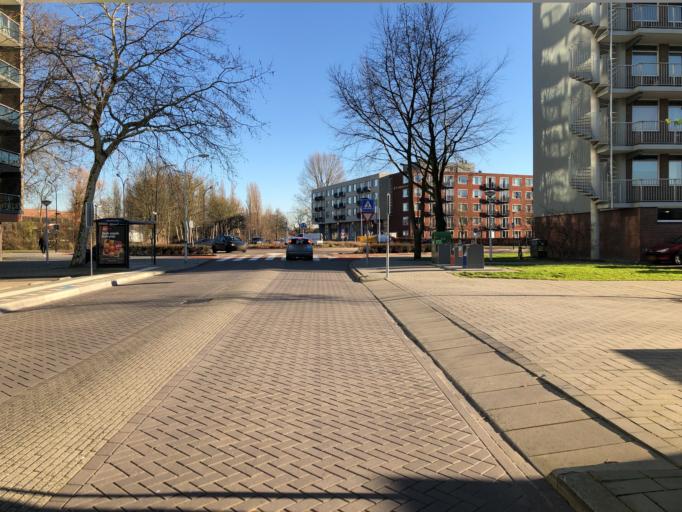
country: NL
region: North Holland
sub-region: Gemeente Uitgeest
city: Uitgeest
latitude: 52.5066
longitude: 4.7608
